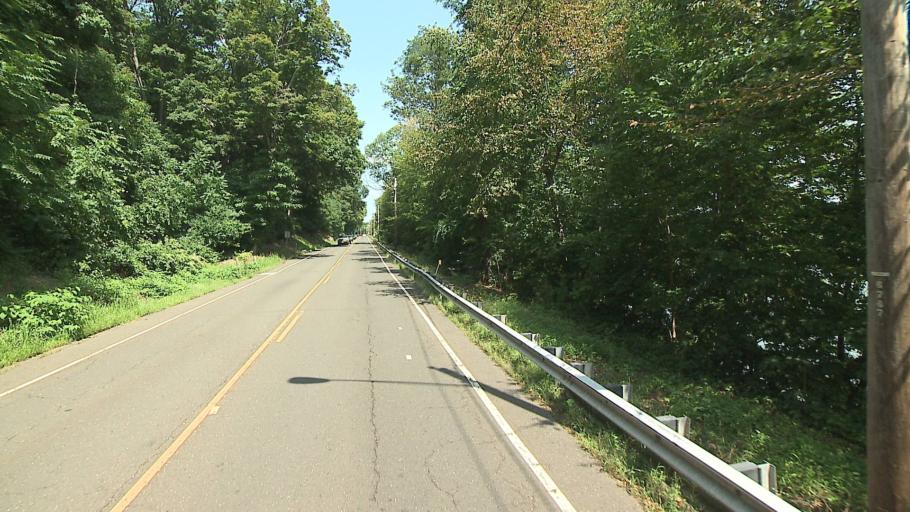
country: US
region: Connecticut
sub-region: New Haven County
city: City of Milford (balance)
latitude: 41.2335
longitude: -73.1088
